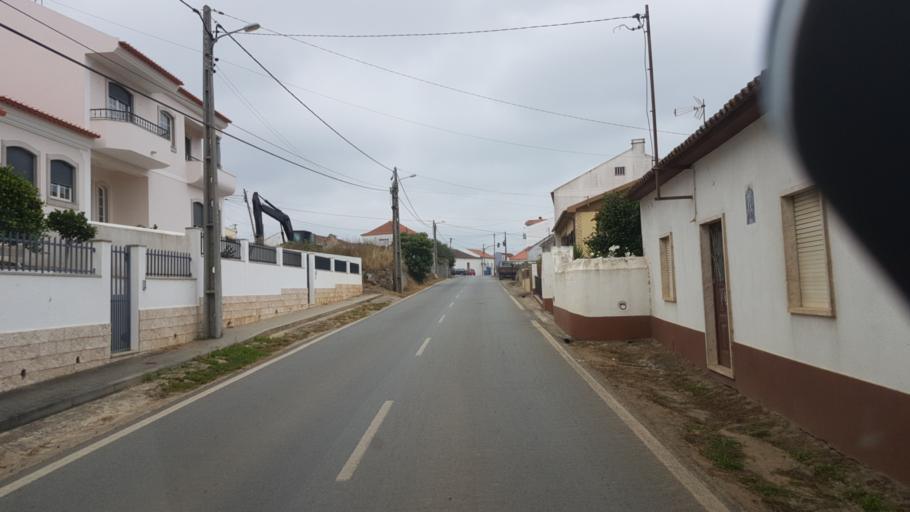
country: PT
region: Leiria
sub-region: Bombarral
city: Bombarral
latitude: 39.2822
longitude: -9.1904
